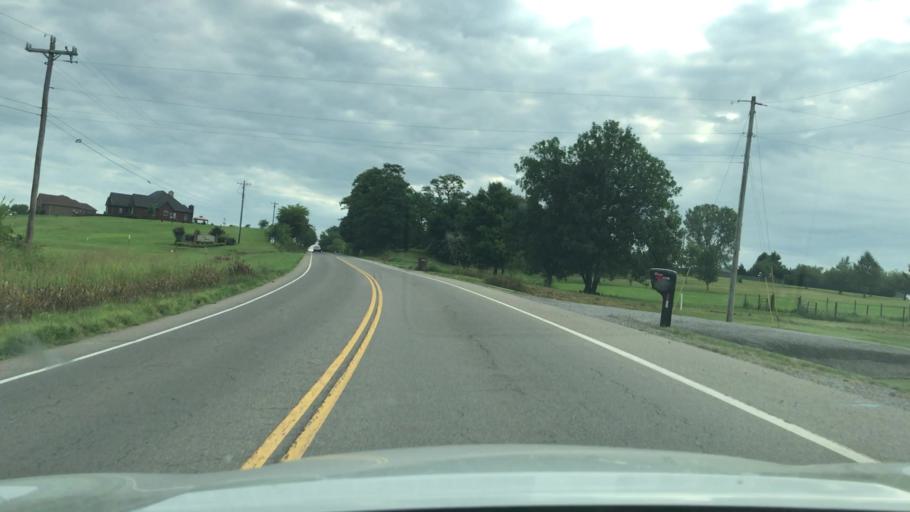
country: US
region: Kentucky
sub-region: Todd County
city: Guthrie
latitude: 36.6278
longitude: -87.2195
